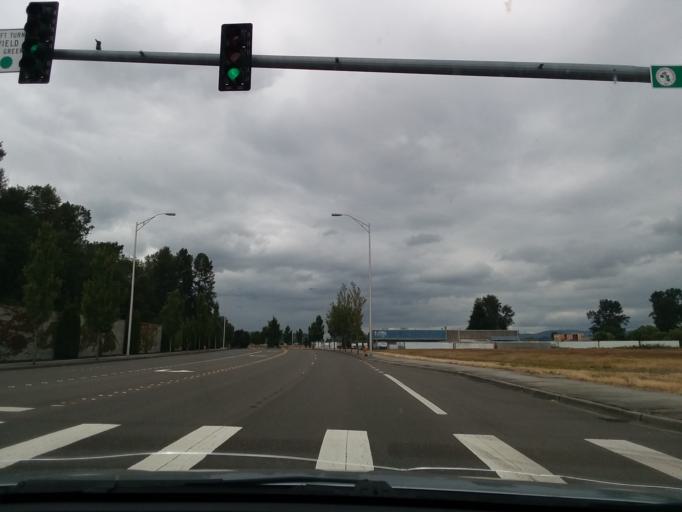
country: US
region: Washington
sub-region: King County
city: SeaTac
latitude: 47.4316
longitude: -122.2657
